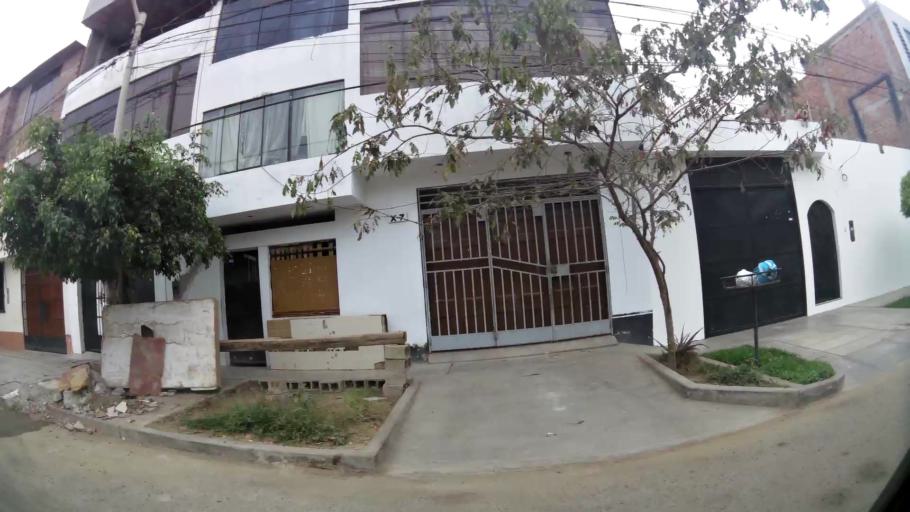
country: PE
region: La Libertad
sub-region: Provincia de Trujillo
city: Trujillo
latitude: -8.1125
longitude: -79.0434
